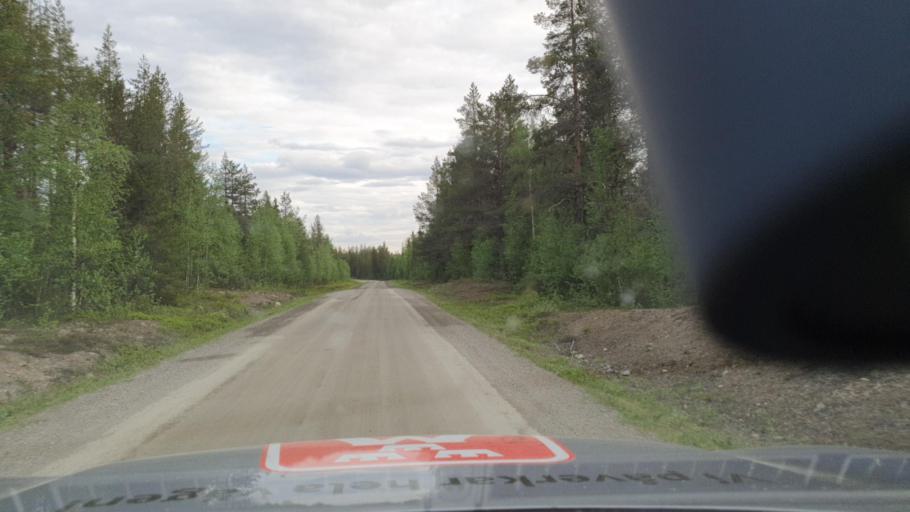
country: SE
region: Norrbotten
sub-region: Gallivare Kommun
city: Gaellivare
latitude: 66.6968
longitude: 21.1643
